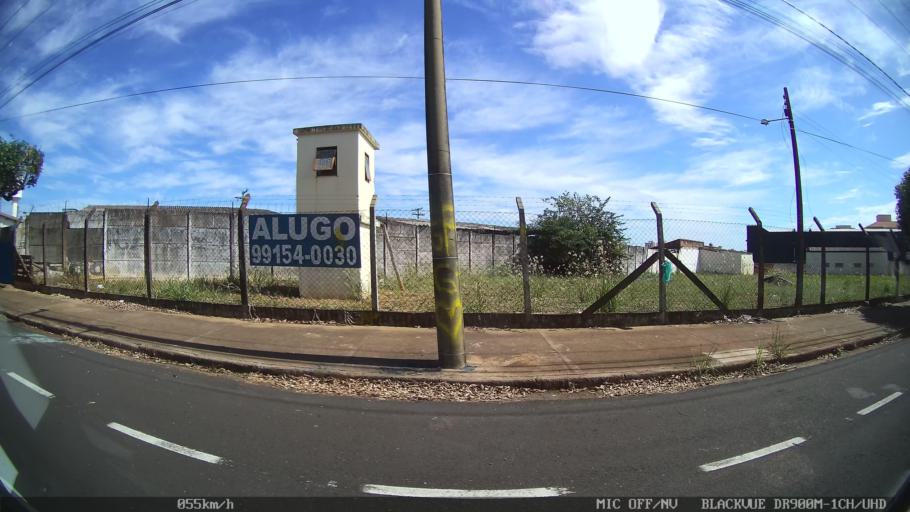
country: BR
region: Sao Paulo
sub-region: Sao Jose Do Rio Preto
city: Sao Jose do Rio Preto
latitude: -20.8301
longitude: -49.3633
